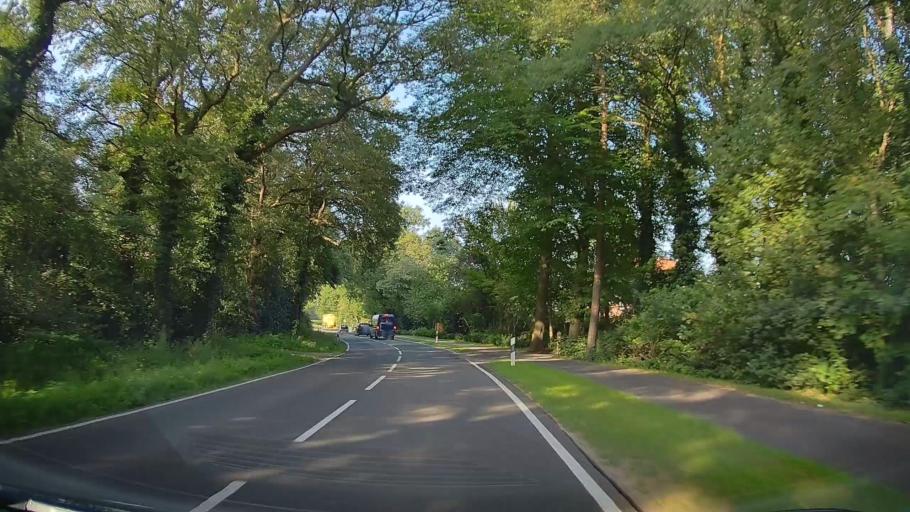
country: DE
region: Lower Saxony
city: Friesoythe
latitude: 53.0904
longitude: 7.8337
